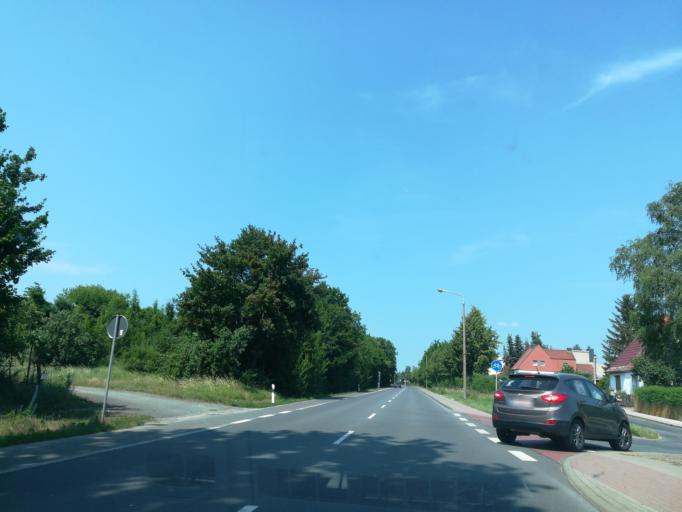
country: DE
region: Saxony-Anhalt
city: Aschersleben
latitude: 51.7715
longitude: 11.4549
